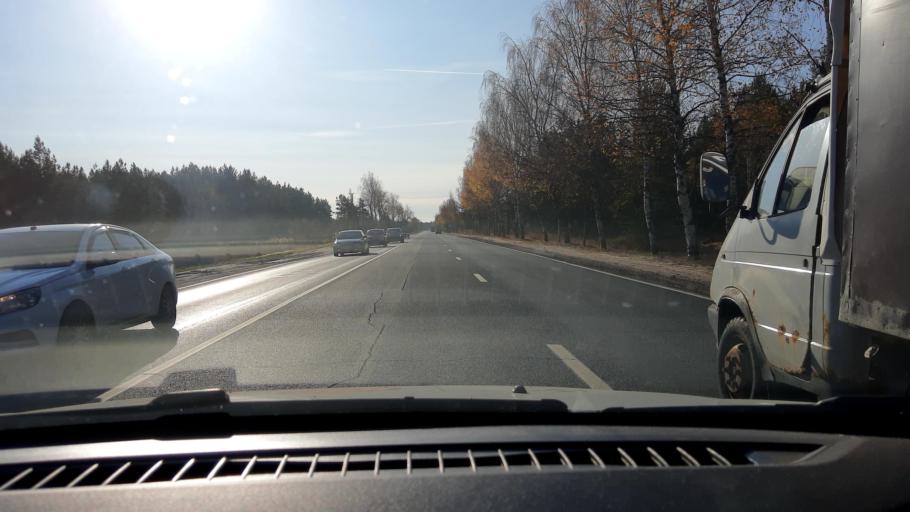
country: RU
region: Nizjnij Novgorod
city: Dzerzhinsk
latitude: 56.2872
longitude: 43.4757
